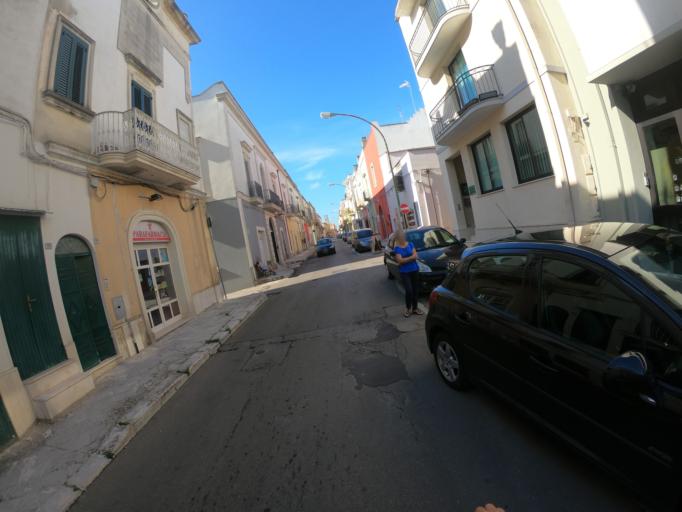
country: IT
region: Apulia
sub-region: Provincia di Lecce
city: Supersano
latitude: 40.0172
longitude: 18.2406
